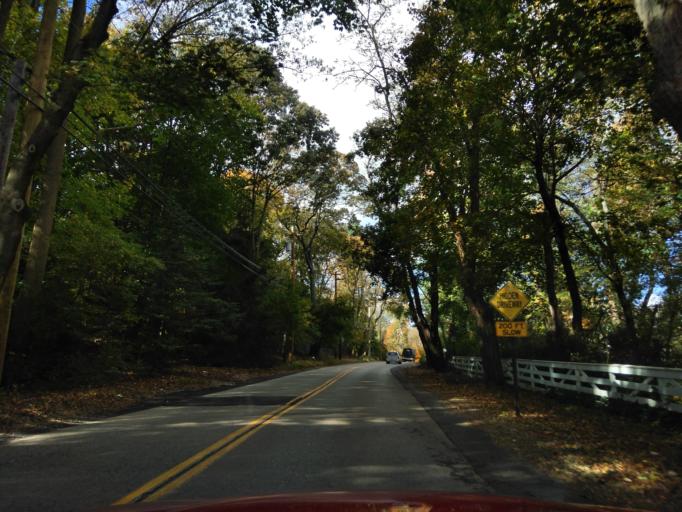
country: US
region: New York
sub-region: Nassau County
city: East Norwich
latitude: 40.8410
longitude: -73.5180
